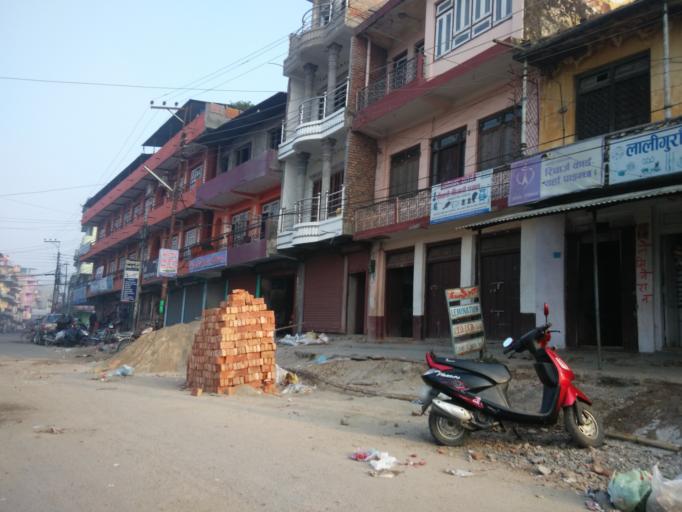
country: NP
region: Central Region
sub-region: Narayani Zone
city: Bharatpur
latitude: 27.6969
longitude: 84.4254
